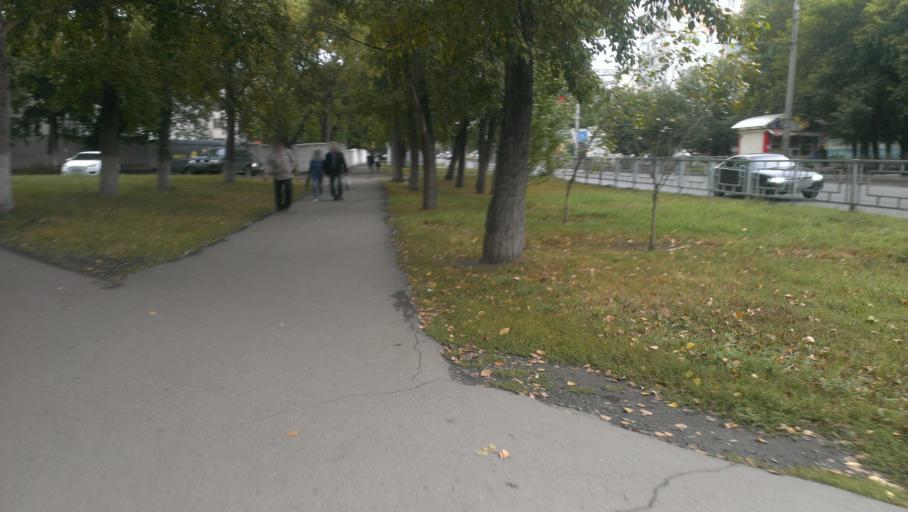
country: RU
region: Altai Krai
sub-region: Gorod Barnaulskiy
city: Barnaul
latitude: 53.3709
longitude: 83.6816
